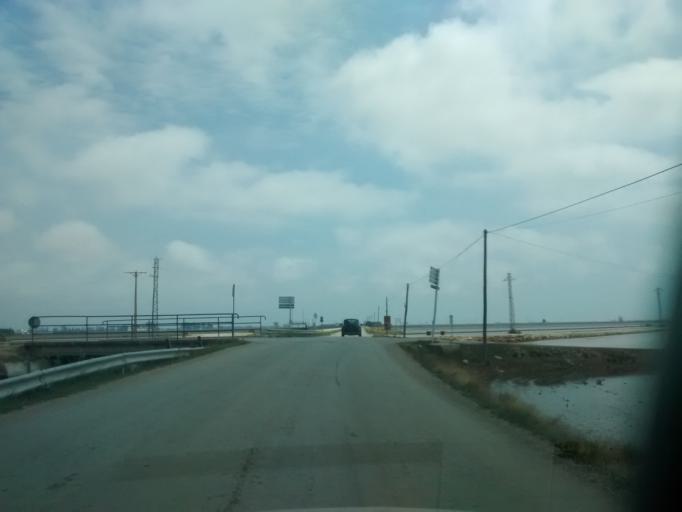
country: ES
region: Catalonia
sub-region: Provincia de Tarragona
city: Deltebre
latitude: 40.7022
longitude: 0.7401
